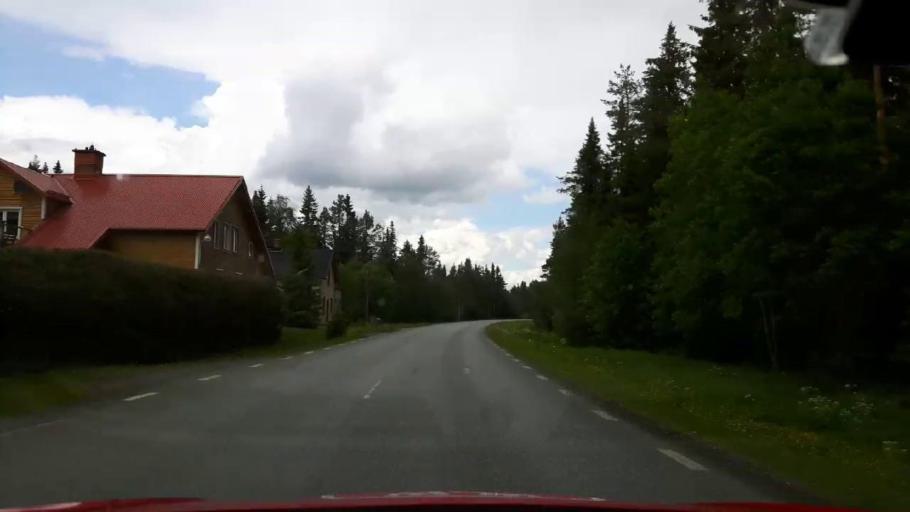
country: SE
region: Jaemtland
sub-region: Krokoms Kommun
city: Krokom
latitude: 63.5011
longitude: 14.2135
